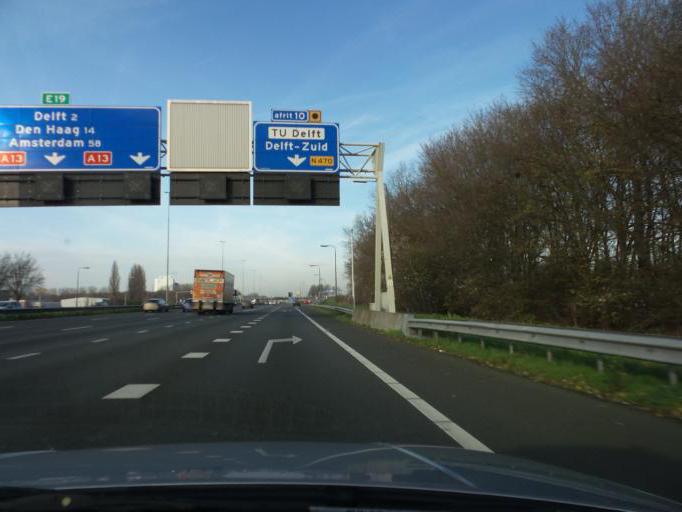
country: NL
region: South Holland
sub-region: Gemeente Delft
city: Delft
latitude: 51.9910
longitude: 4.3916
